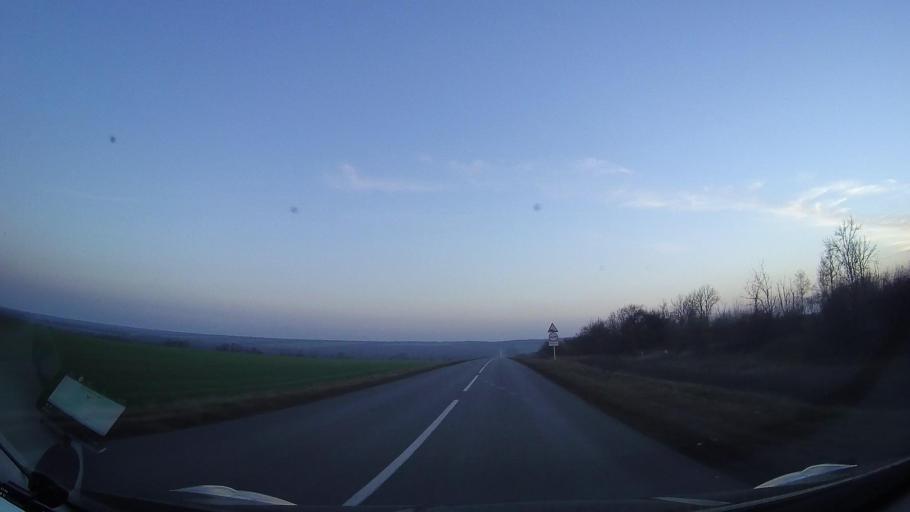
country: RU
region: Rostov
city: Zernograd
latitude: 46.9085
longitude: 40.3388
